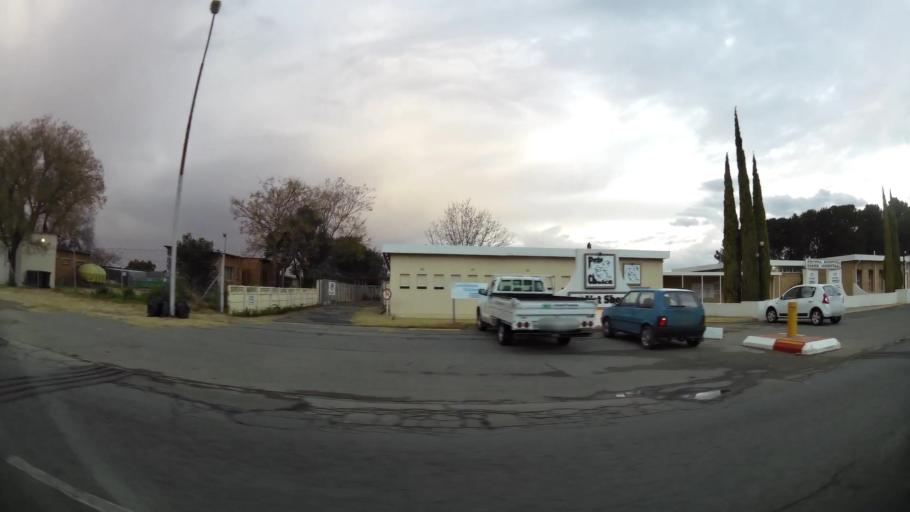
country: ZA
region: Orange Free State
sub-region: Lejweleputswa District Municipality
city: Welkom
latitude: -27.9546
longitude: 26.7582
